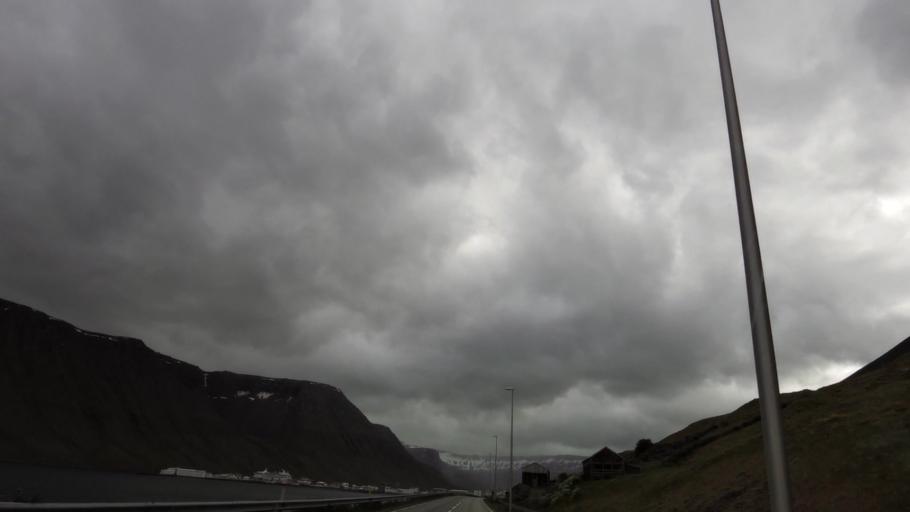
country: IS
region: Westfjords
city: Isafjoerdur
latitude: 66.0860
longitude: -23.1195
